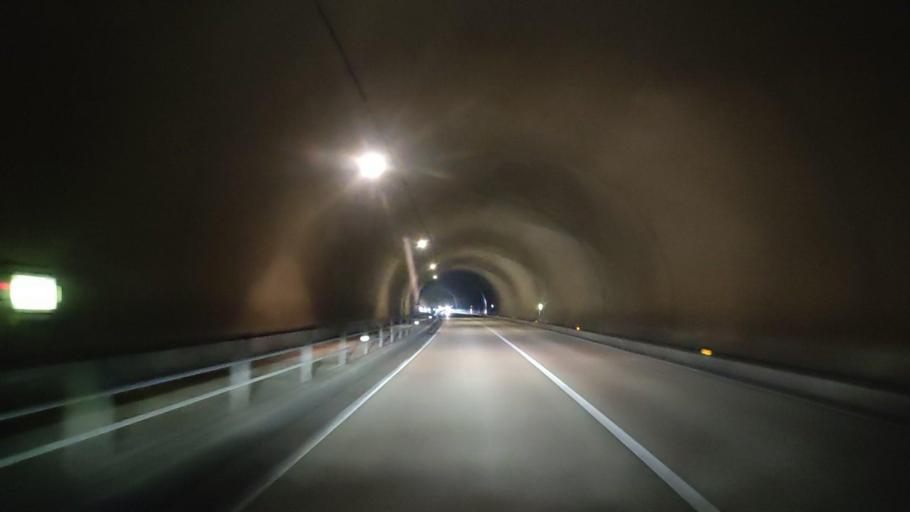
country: JP
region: Gifu
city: Godo
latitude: 35.5897
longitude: 136.6300
